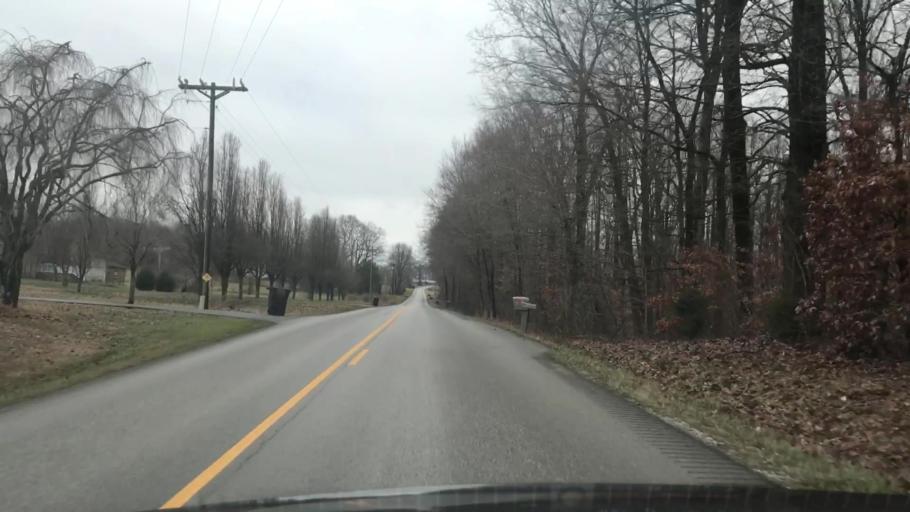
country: US
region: Kentucky
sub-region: Barren County
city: Glasgow
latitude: 36.8818
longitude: -85.7906
